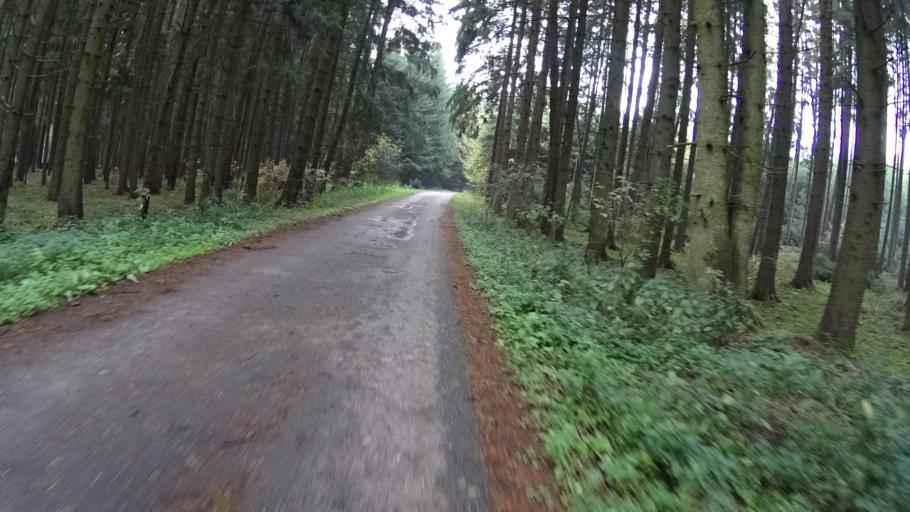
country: DE
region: Bavaria
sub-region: Upper Bavaria
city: Buxheim
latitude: 48.8354
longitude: 11.2678
